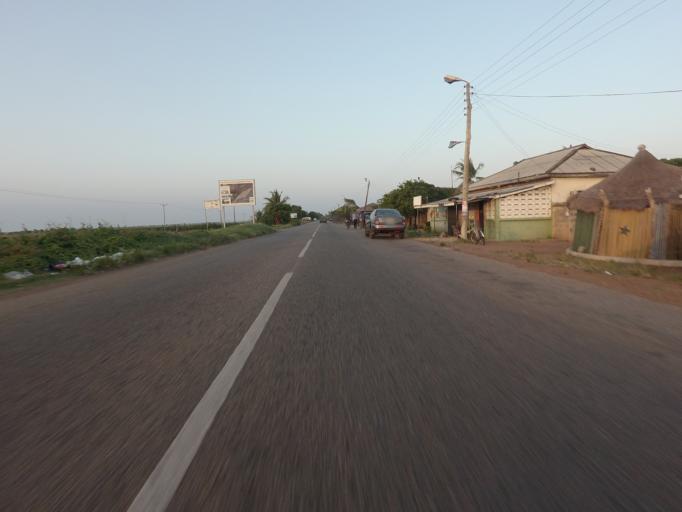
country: GH
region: Volta
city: Anloga
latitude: 5.7979
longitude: 0.9088
